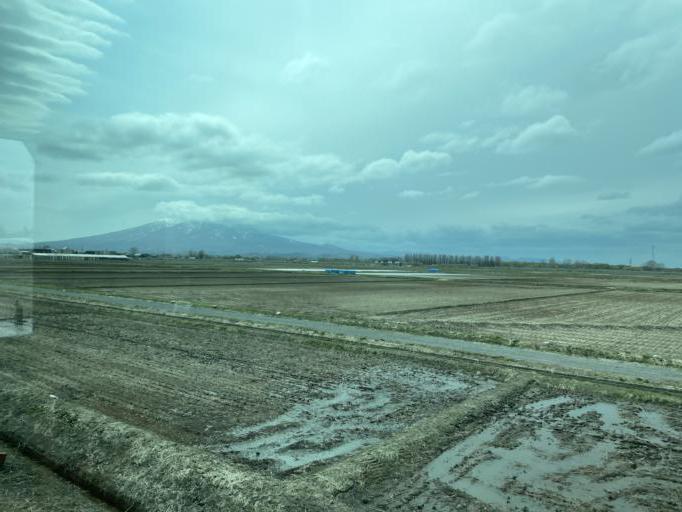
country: JP
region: Aomori
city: Goshogawara
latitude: 40.7735
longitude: 140.4340
